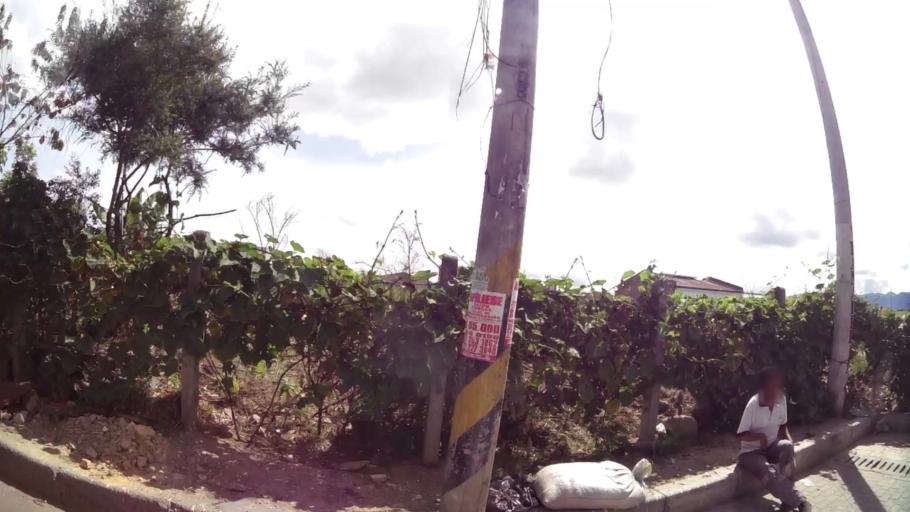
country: CO
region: Bogota D.C.
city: Bogota
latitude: 4.6563
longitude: -74.1361
